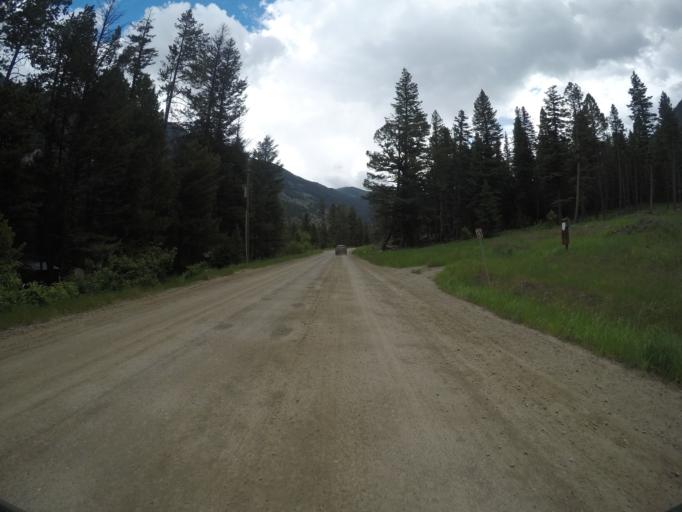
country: US
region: Montana
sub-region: Park County
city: Livingston
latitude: 45.4904
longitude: -110.2208
